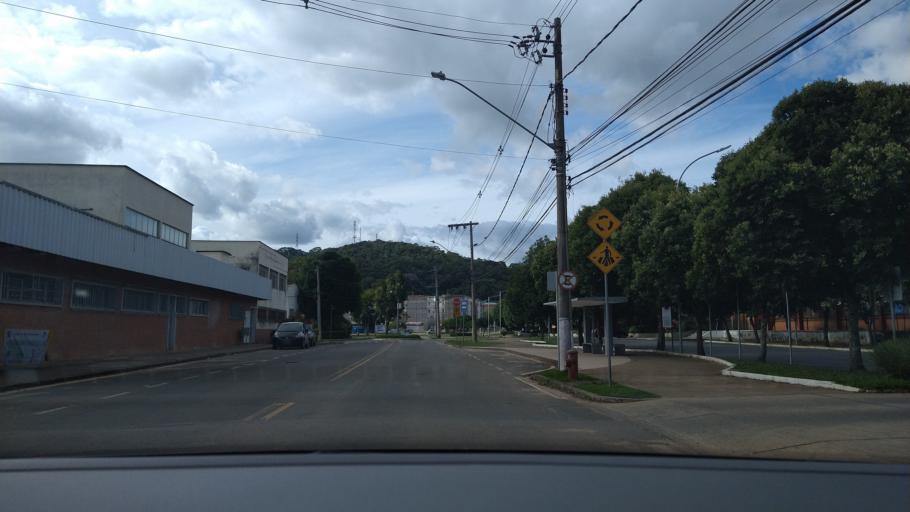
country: BR
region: Minas Gerais
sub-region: Vicosa
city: Vicosa
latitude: -20.7653
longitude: -42.8691
